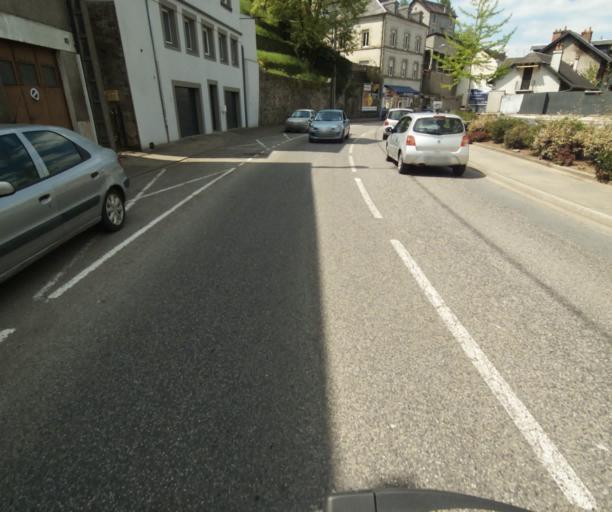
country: FR
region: Limousin
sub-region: Departement de la Correze
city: Tulle
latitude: 45.2574
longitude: 1.7536
